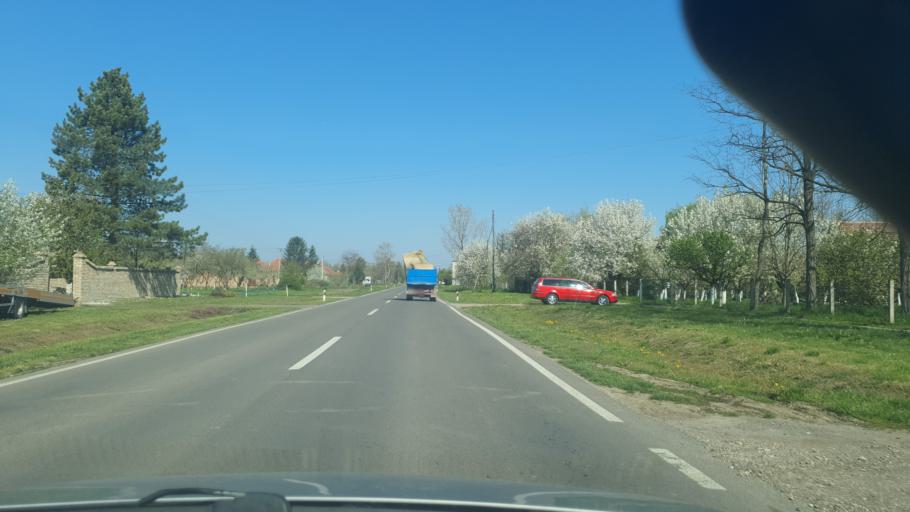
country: RS
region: Autonomna Pokrajina Vojvodina
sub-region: Zapadnobacki Okrug
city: Sombor
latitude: 45.8021
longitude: 19.0569
